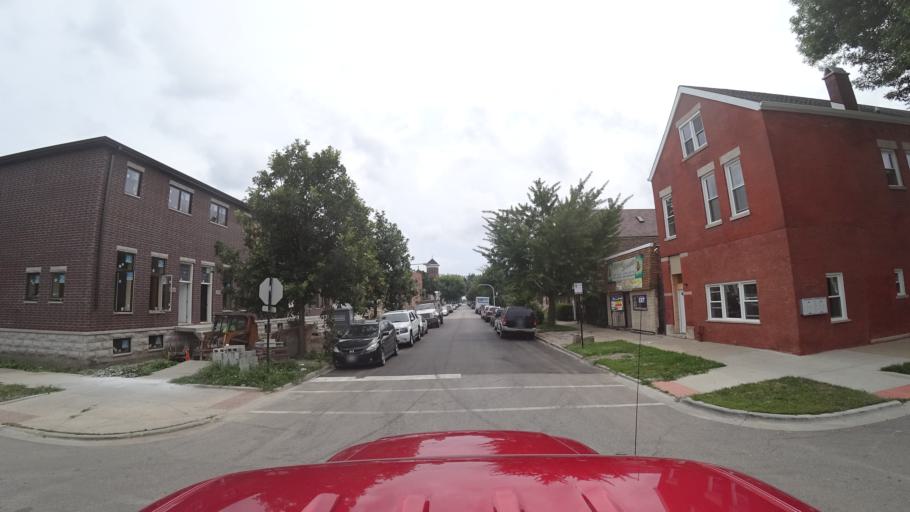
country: US
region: Illinois
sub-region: Cook County
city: Chicago
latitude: 41.8250
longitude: -87.6702
